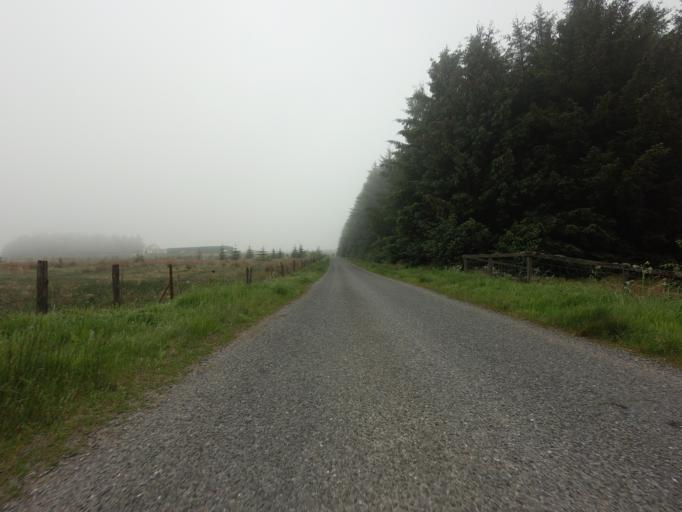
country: GB
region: Scotland
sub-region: Perth and Kinross
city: Kinross
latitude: 56.1504
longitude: -3.4536
